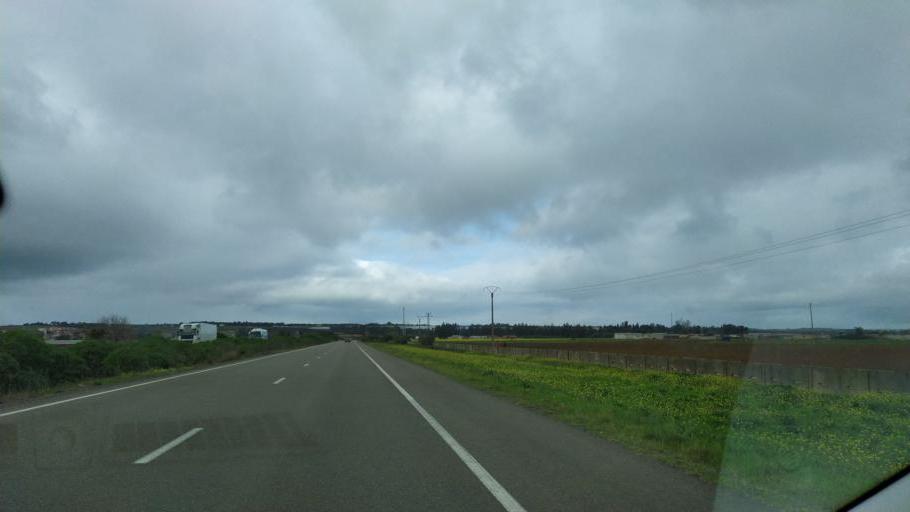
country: MA
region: Gharb-Chrarda-Beni Hssen
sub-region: Kenitra Province
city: Kenitra
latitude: 34.4012
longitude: -6.5197
